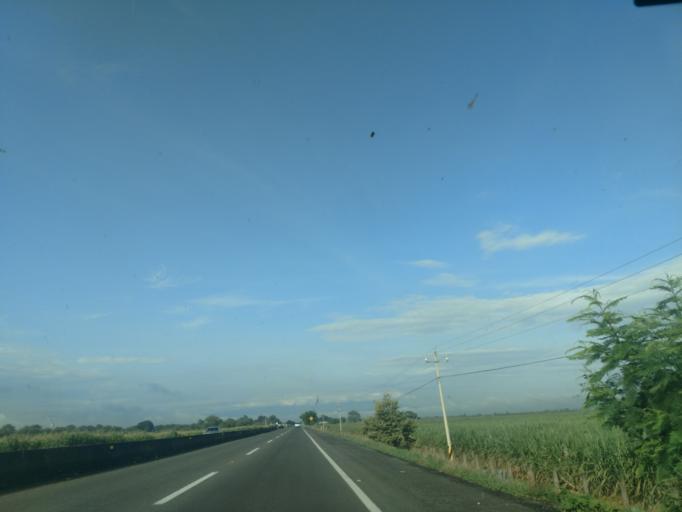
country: MX
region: Jalisco
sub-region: Ameca
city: Los Pocitos
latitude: 20.5547
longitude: -103.8894
